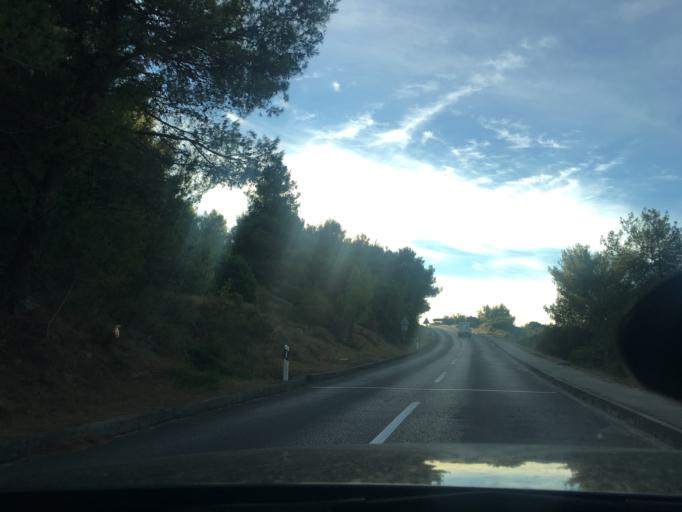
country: HR
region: Splitsko-Dalmatinska
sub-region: Grad Vis
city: Vis
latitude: 43.0567
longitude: 16.1920
